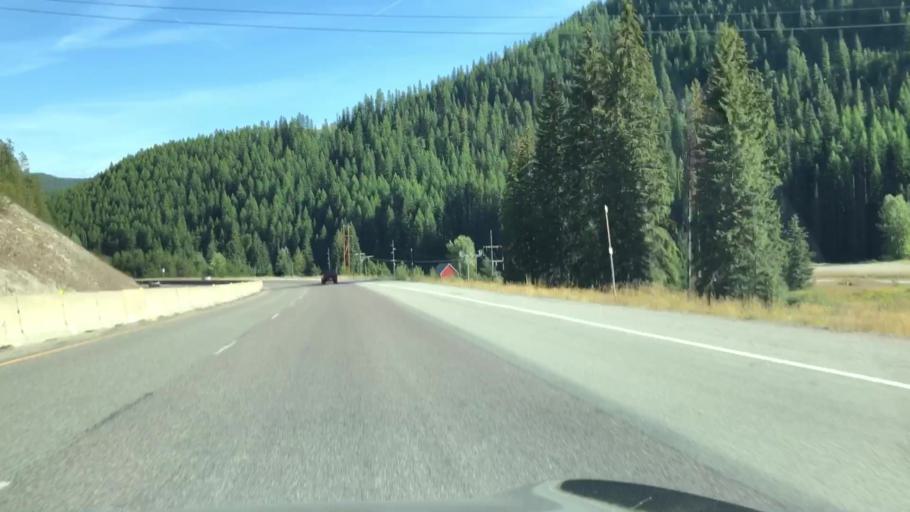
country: US
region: Montana
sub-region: Sanders County
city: Thompson Falls
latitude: 47.4200
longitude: -115.6030
